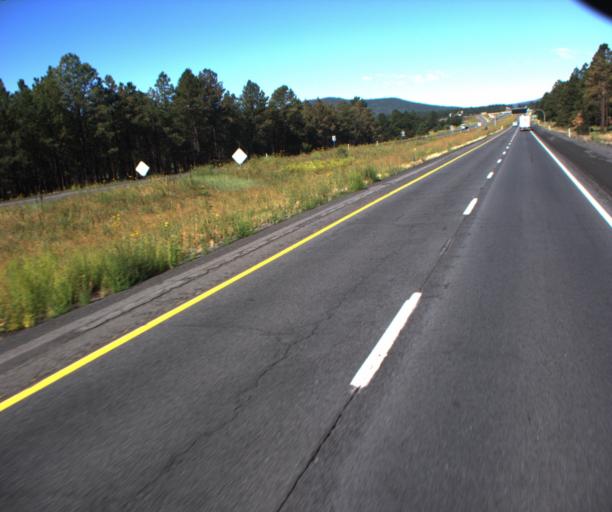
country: US
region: Arizona
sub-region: Coconino County
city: Williams
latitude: 35.2585
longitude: -112.1097
